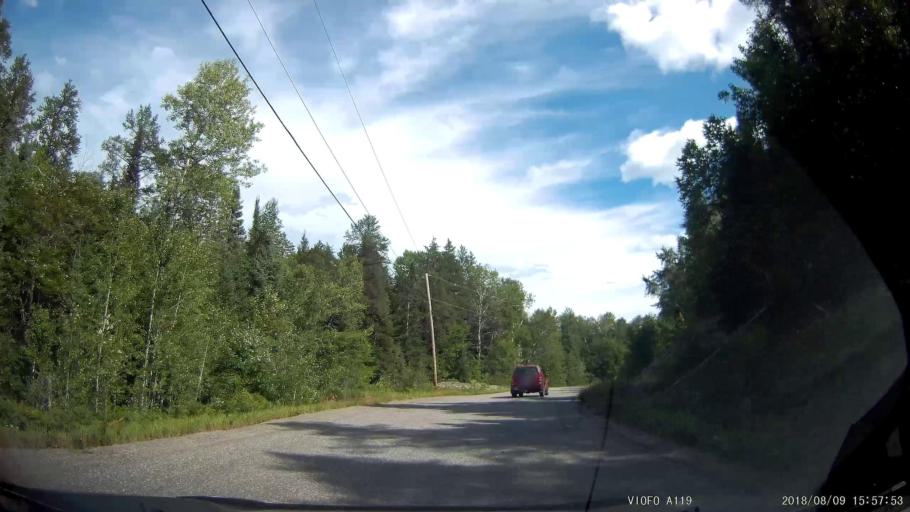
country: CA
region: Ontario
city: Rayside-Balfour
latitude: 46.6074
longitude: -81.5015
